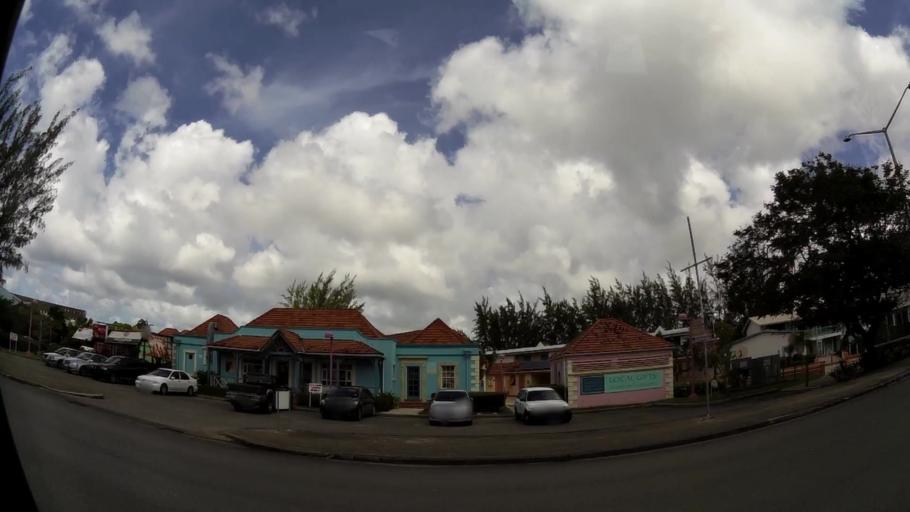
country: BB
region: Saint Michael
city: Bridgetown
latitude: 13.0985
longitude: -59.6240
